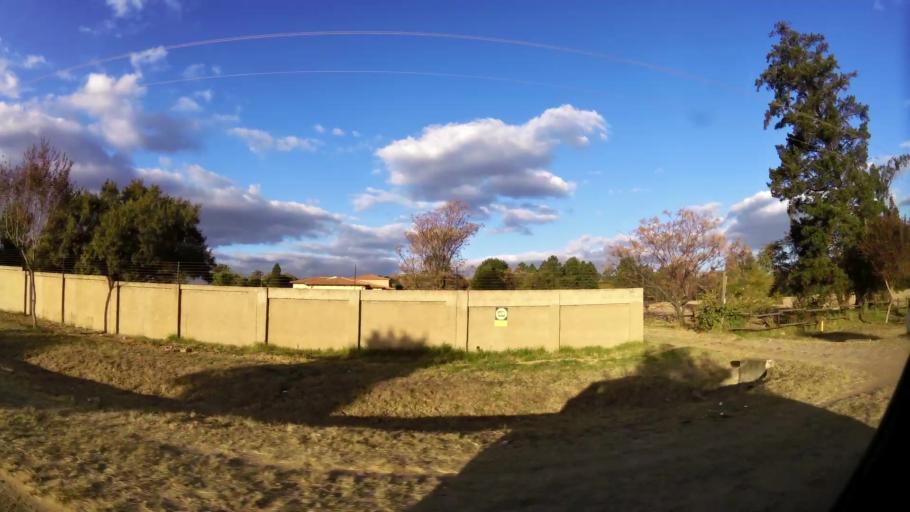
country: ZA
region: Gauteng
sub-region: City of Johannesburg Metropolitan Municipality
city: Midrand
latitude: -25.9625
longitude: 28.1537
